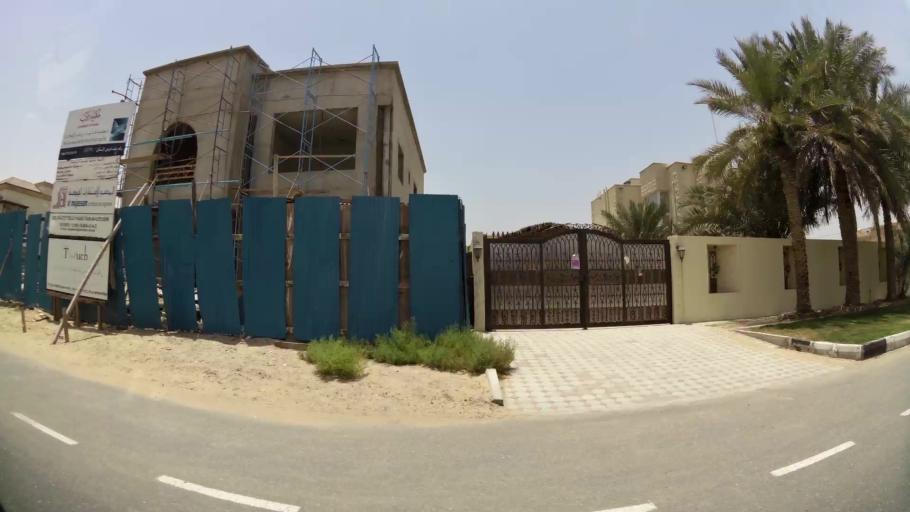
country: AE
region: Ash Shariqah
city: Sharjah
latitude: 25.2115
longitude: 55.3880
